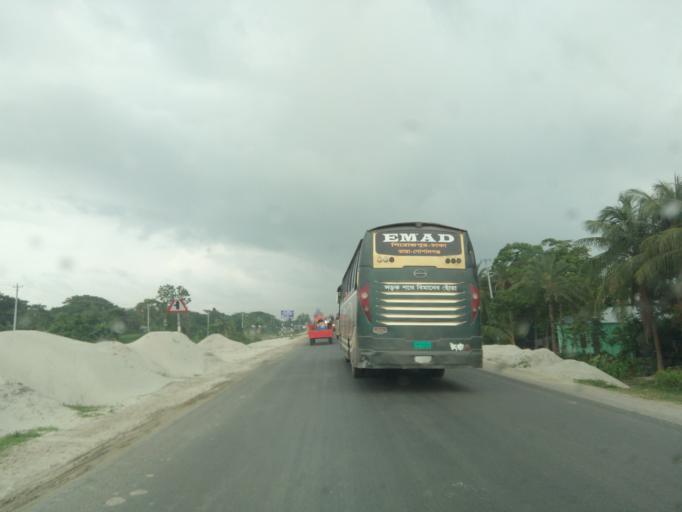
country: BD
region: Dhaka
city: Char Bhadrasan
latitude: 23.3695
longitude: 90.0661
